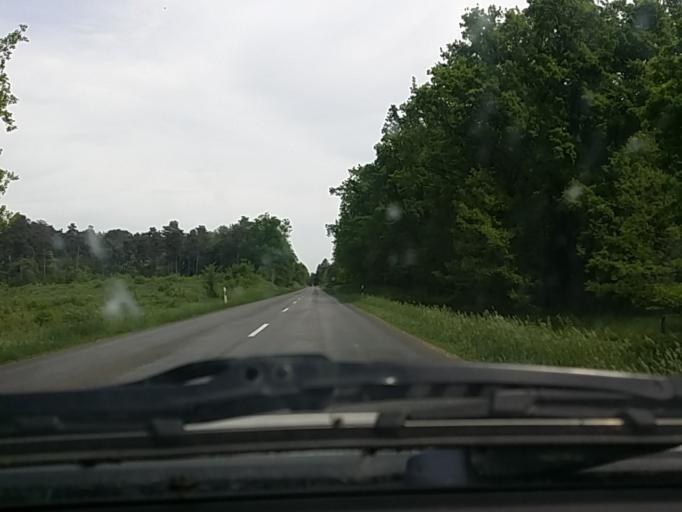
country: HU
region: Somogy
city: Barcs
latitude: 45.9639
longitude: 17.5080
